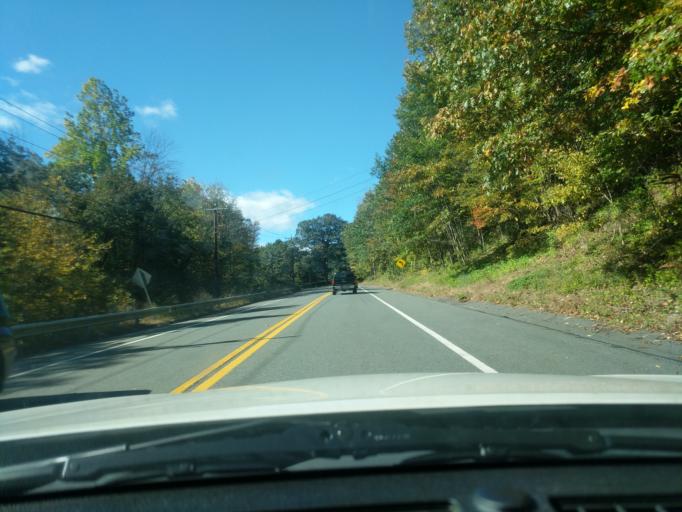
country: US
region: Massachusetts
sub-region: Hampden County
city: Granville
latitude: 42.1642
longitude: -72.8457
